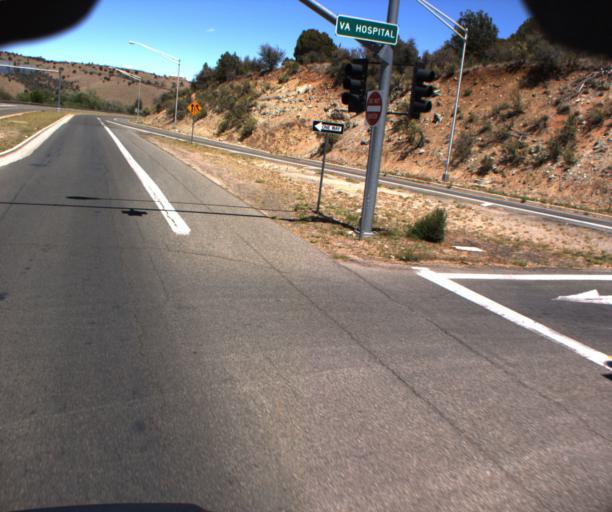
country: US
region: Arizona
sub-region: Yavapai County
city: Prescott
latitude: 34.5507
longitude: -112.4498
